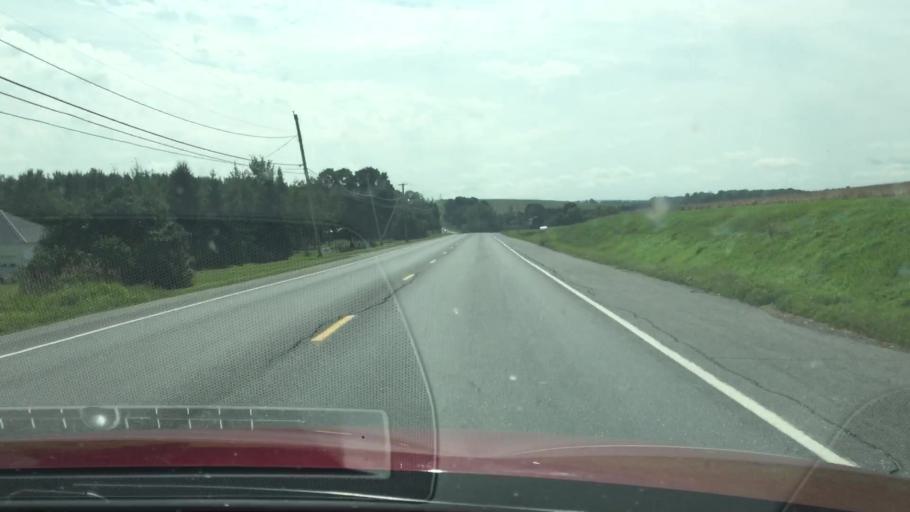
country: US
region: Maine
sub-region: Aroostook County
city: Easton
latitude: 46.5884
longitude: -67.9618
